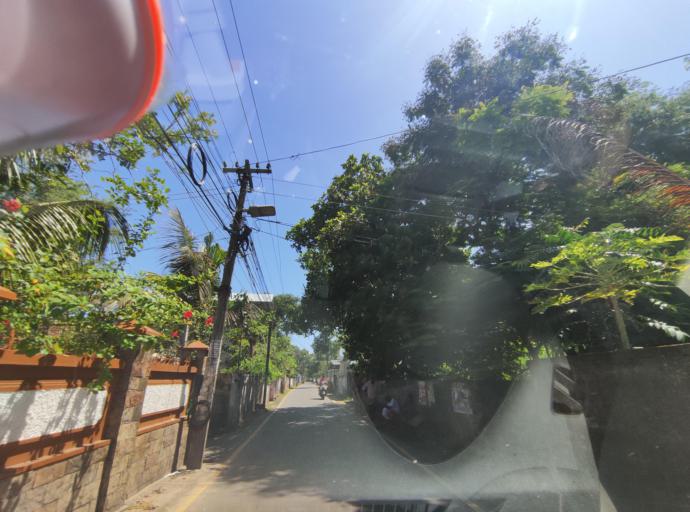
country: IN
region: Kerala
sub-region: Alappuzha
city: Alleppey
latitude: 9.4766
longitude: 76.3309
